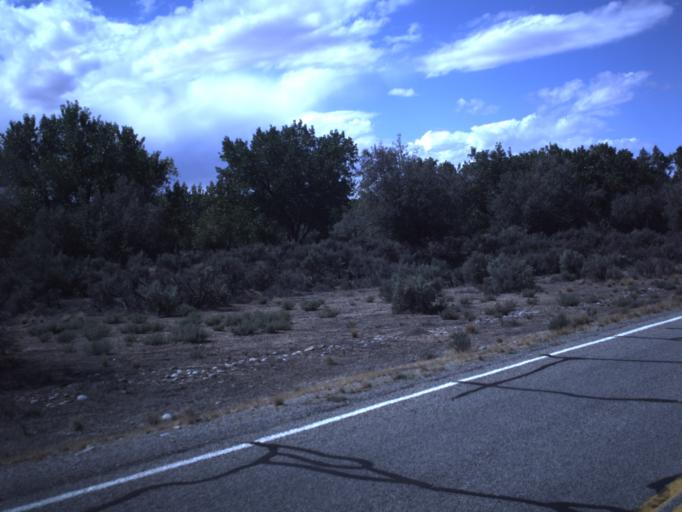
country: US
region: Utah
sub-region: San Juan County
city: Blanding
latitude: 37.2821
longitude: -109.5104
